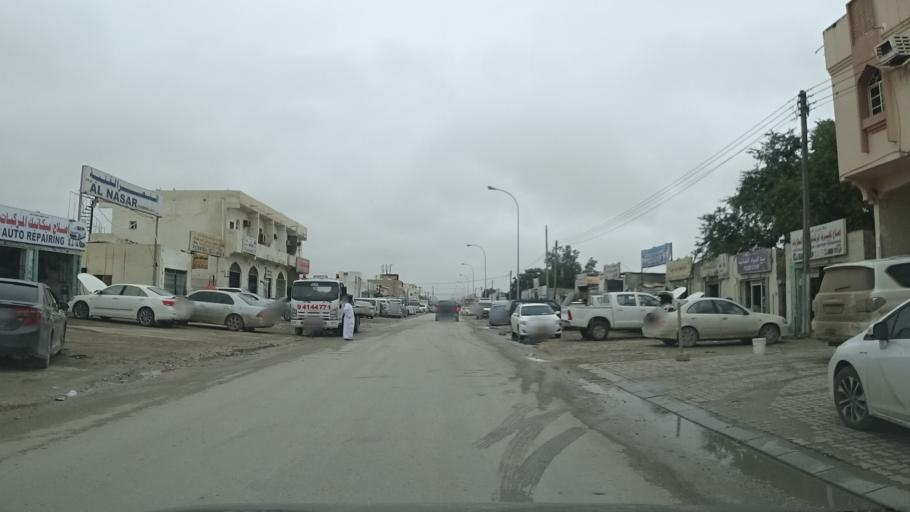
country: OM
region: Zufar
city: Salalah
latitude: 17.0177
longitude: 54.0459
